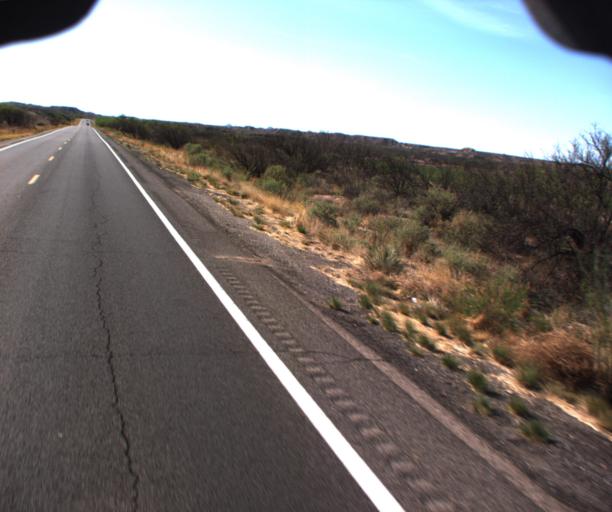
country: US
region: Arizona
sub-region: Cochise County
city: Saint David
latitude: 31.8429
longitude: -110.1918
